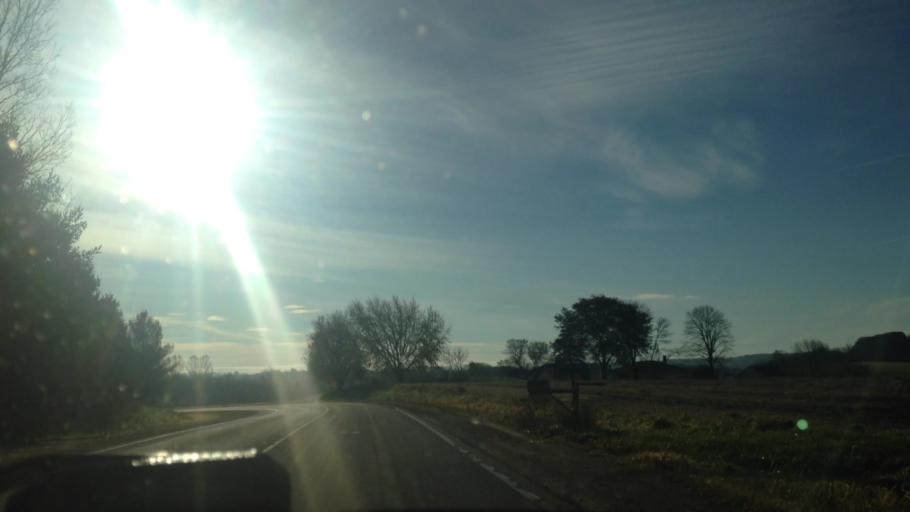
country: US
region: Wisconsin
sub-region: Dodge County
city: Mayville
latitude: 43.4802
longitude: -88.5064
